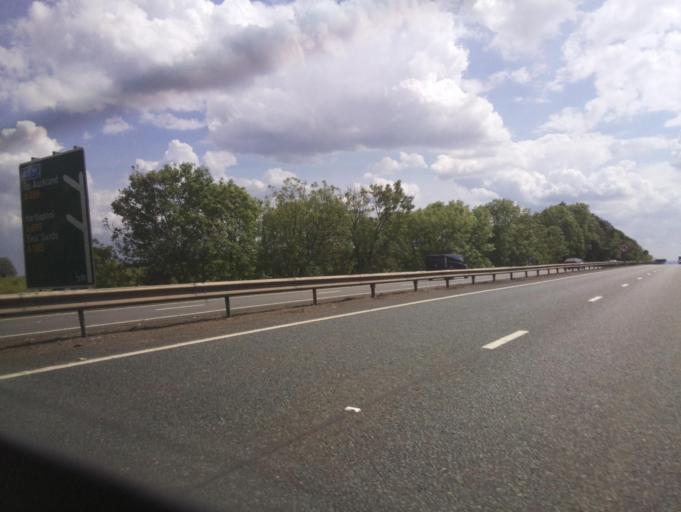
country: GB
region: England
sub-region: Hartlepool
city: Elwick
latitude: 54.6500
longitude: -1.3021
